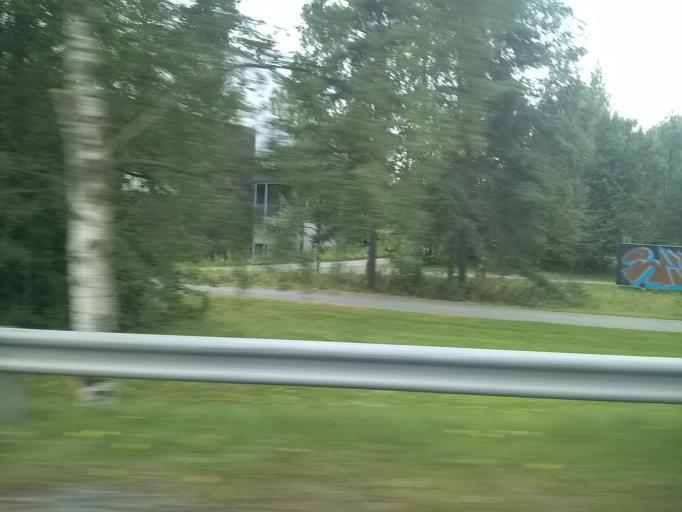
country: FI
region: Pirkanmaa
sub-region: Tampere
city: Tampere
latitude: 61.4949
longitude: 23.8195
